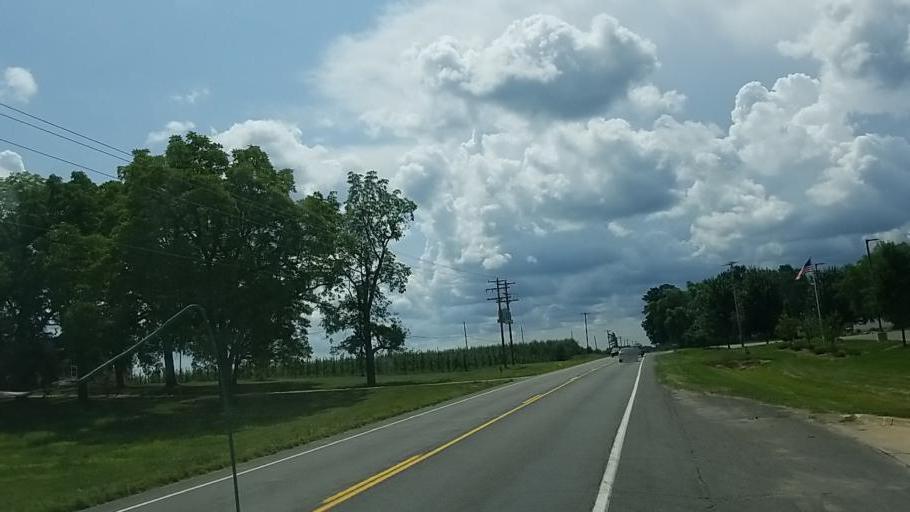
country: US
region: Michigan
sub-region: Kent County
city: Sparta
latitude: 43.1118
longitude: -85.7685
